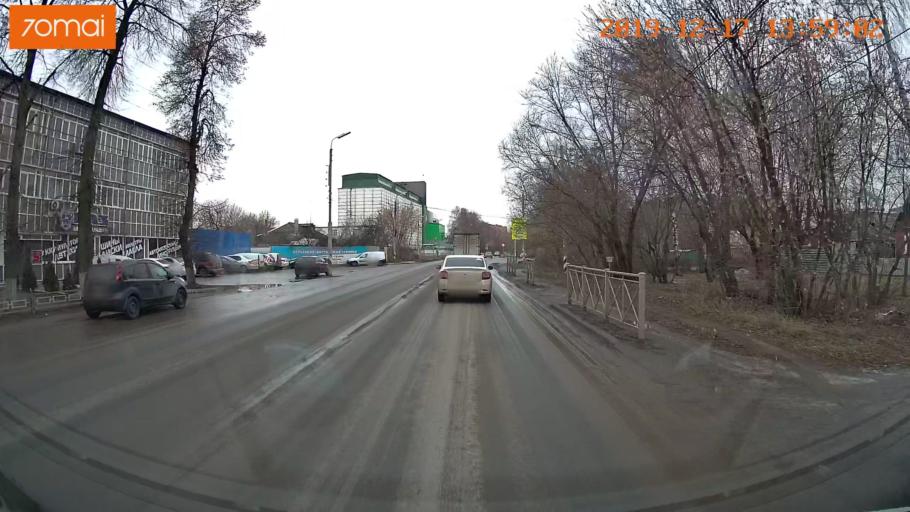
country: RU
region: Rjazan
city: Ryazan'
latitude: 54.6216
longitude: 39.6803
